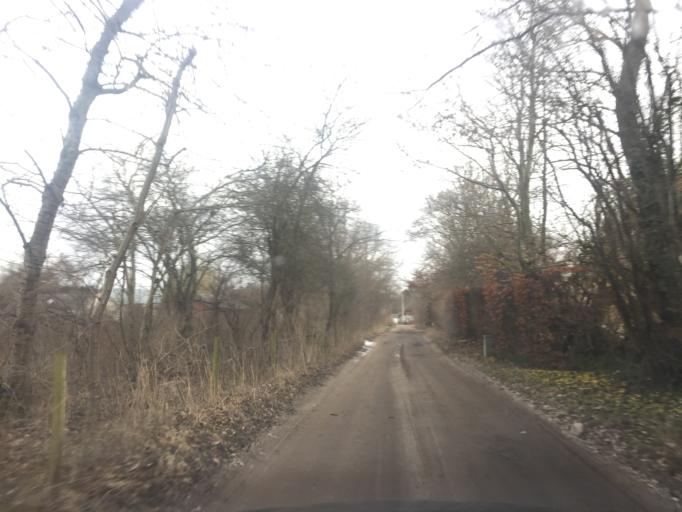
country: DK
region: Capital Region
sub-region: Hoje-Taastrup Kommune
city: Taastrup
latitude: 55.6848
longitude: 12.2690
